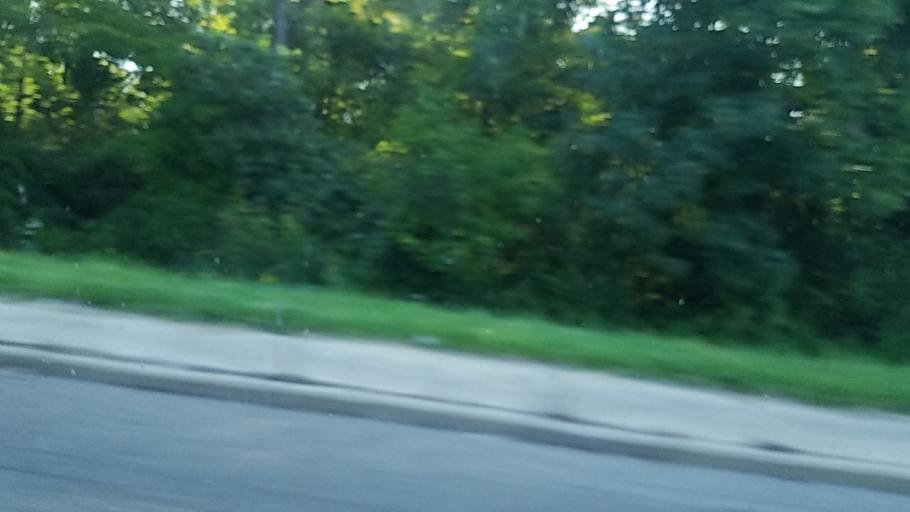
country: US
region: Ohio
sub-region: Trumbull County
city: Niles
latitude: 41.1704
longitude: -80.7527
